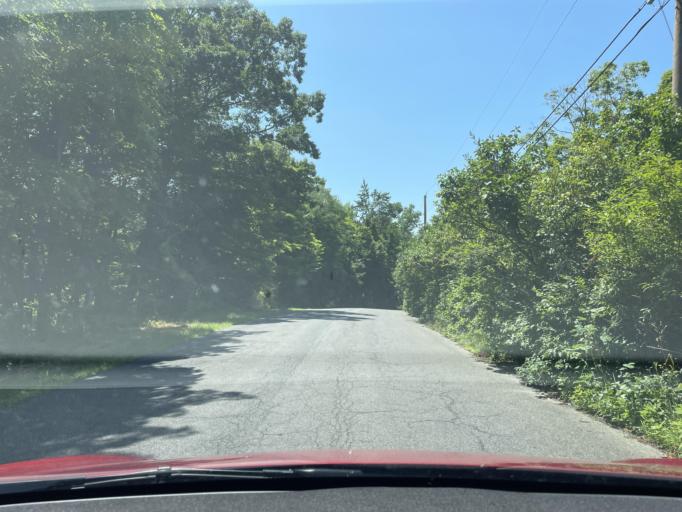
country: US
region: New York
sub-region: Ulster County
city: Lake Katrine
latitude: 42.0020
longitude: -73.9816
